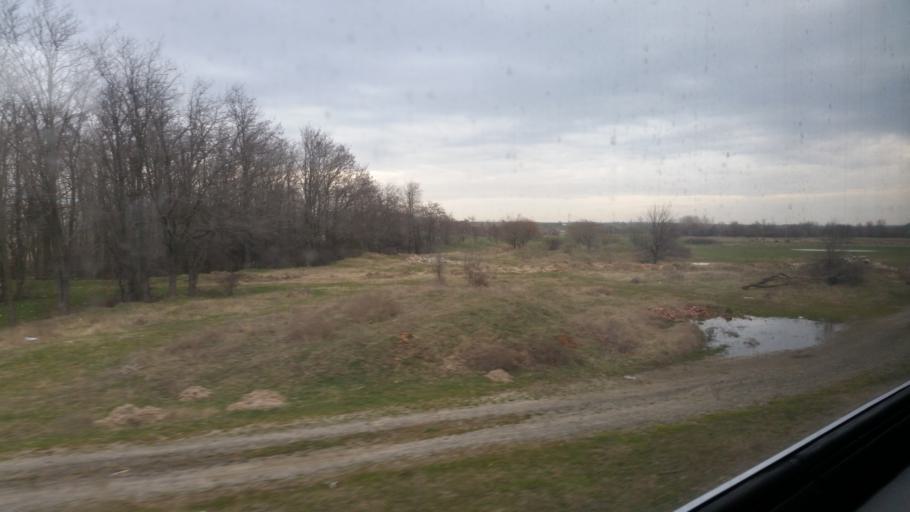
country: TR
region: Tekirdag
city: Velimese
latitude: 41.2507
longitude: 27.8904
